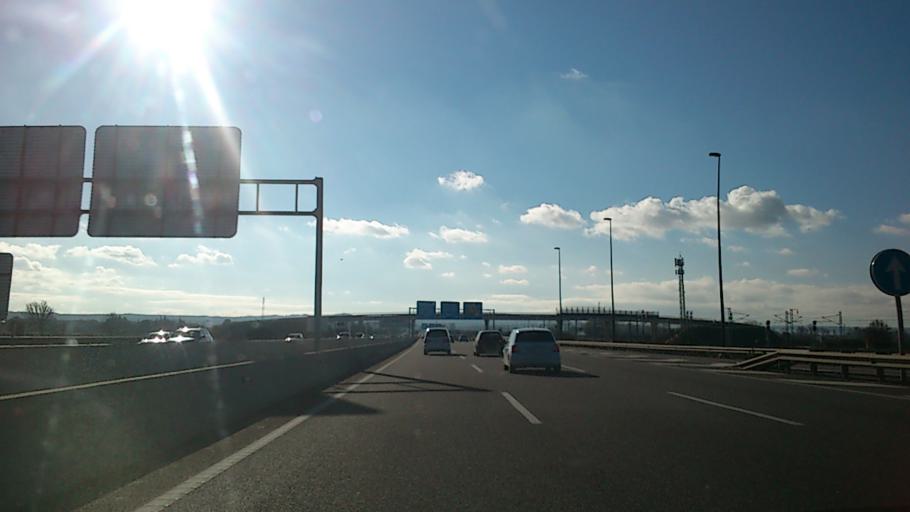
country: ES
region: Aragon
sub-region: Provincia de Zaragoza
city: Oliver-Valdefierro, Oliver, Valdefierro
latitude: 41.6552
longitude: -0.9562
